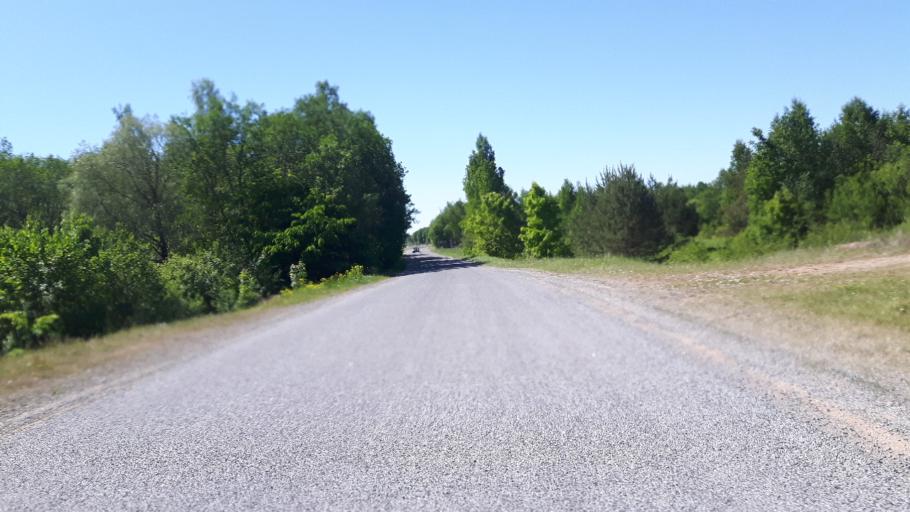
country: EE
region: Ida-Virumaa
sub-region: Sillamaee linn
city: Sillamae
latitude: 59.3758
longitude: 27.8553
